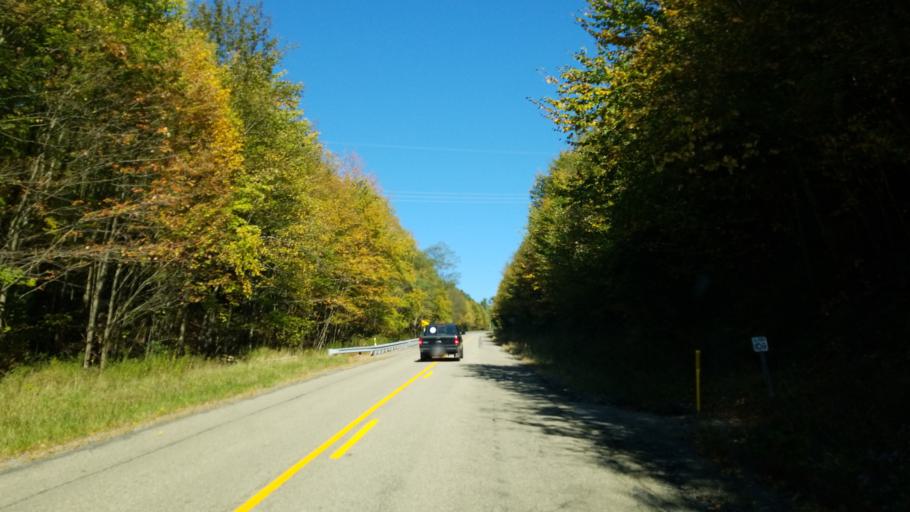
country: US
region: Pennsylvania
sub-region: Clearfield County
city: Shiloh
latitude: 41.2511
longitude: -78.3734
